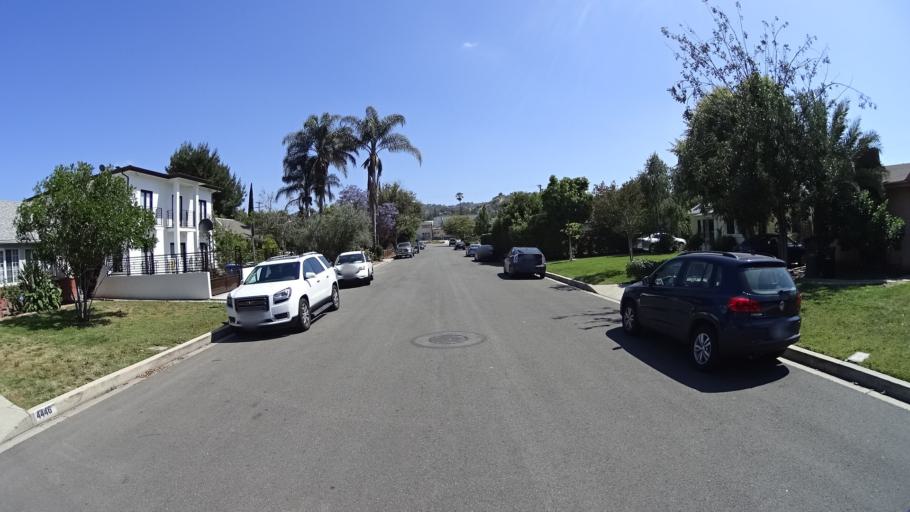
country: US
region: California
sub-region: Los Angeles County
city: Sherman Oaks
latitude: 34.1522
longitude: -118.4433
